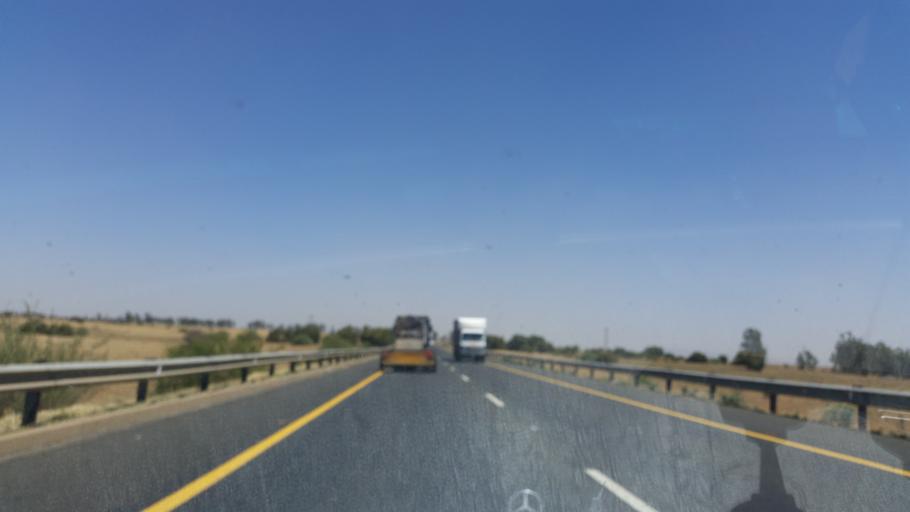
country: ZA
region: Orange Free State
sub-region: Lejweleputswa District Municipality
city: Winburg
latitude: -28.6340
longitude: 26.9001
